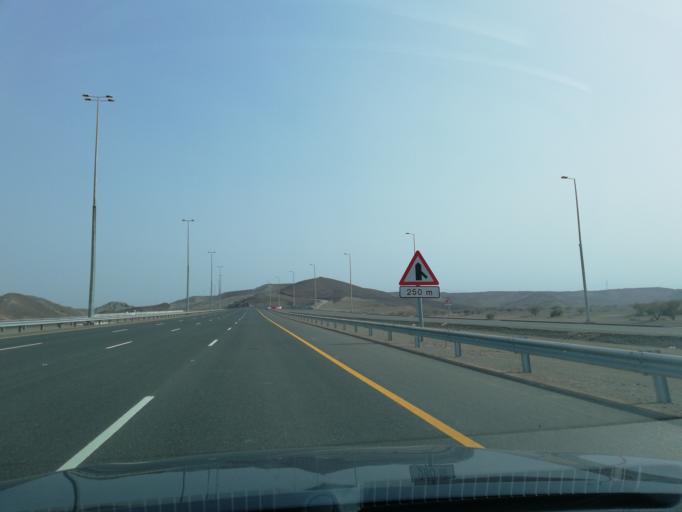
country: OM
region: Al Batinah
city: Al Liwa'
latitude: 24.3595
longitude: 56.5507
